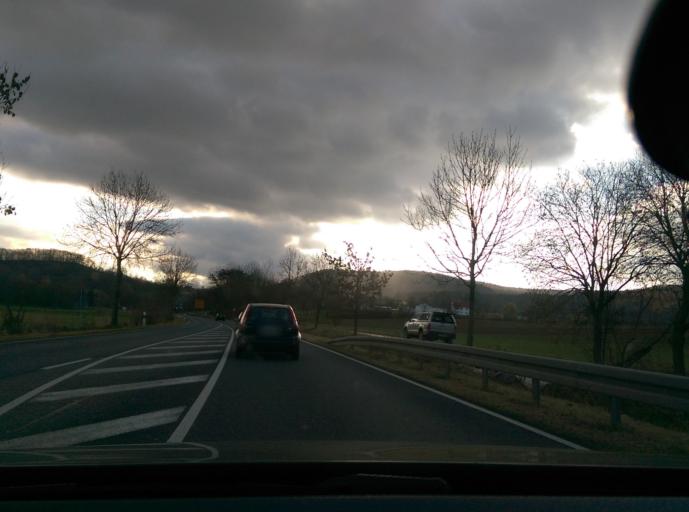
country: DE
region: Thuringia
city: Lindewerra
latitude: 51.3139
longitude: 9.9193
